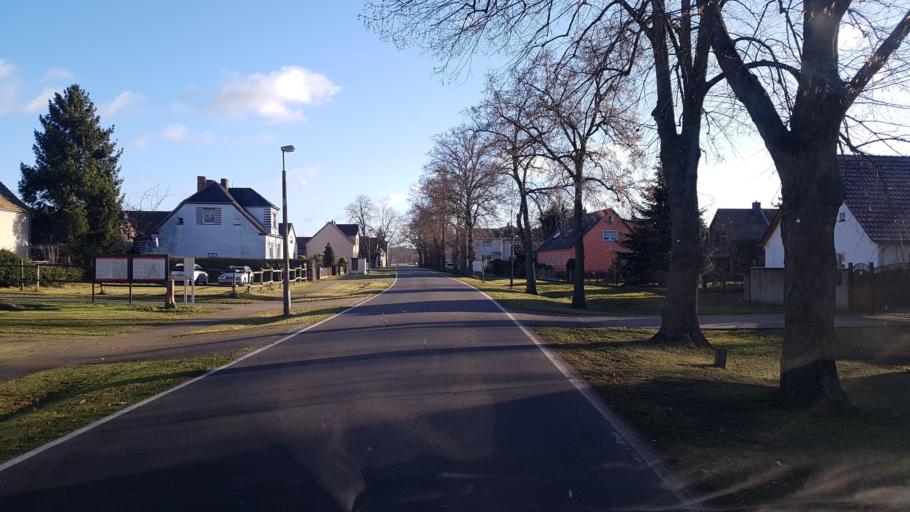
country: DE
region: Brandenburg
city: Forst
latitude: 51.7680
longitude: 14.5944
